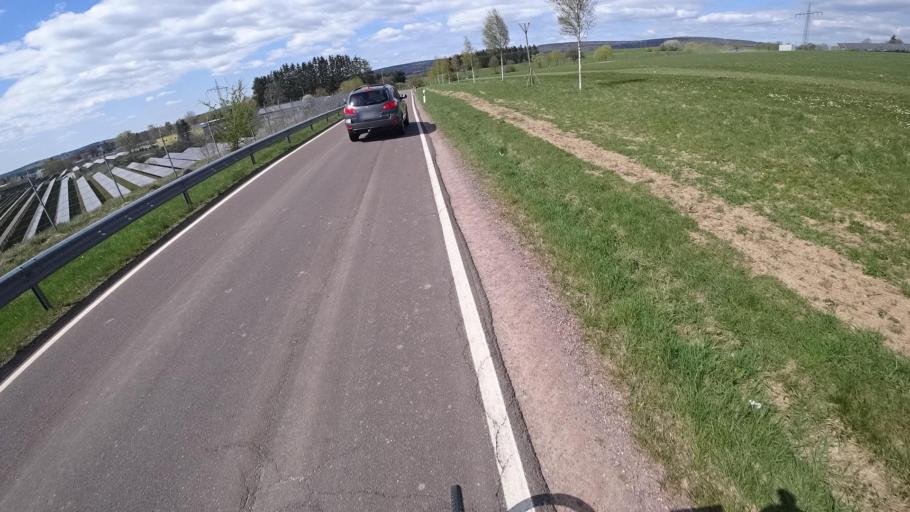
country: DE
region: Rheinland-Pfalz
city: Kell
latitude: 49.6340
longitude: 6.8408
